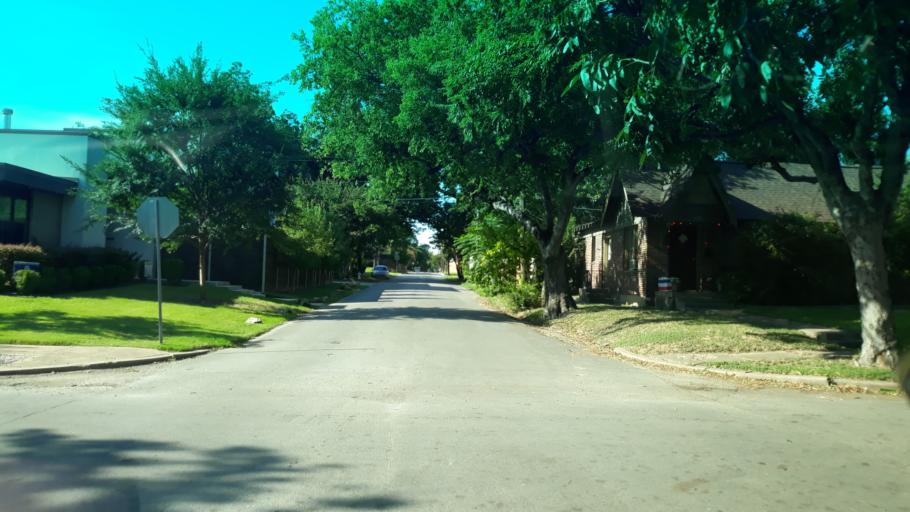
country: US
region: Texas
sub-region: Dallas County
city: Highland Park
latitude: 32.8210
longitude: -96.7560
